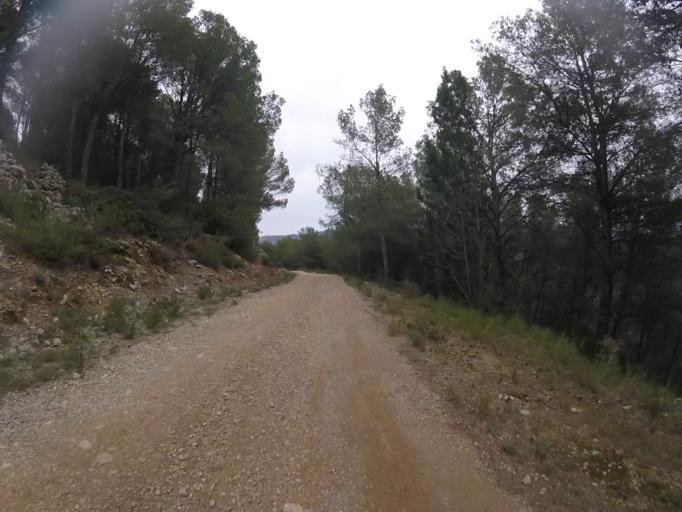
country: ES
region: Valencia
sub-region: Provincia de Castello
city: Alcala de Xivert
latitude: 40.3121
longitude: 0.2648
